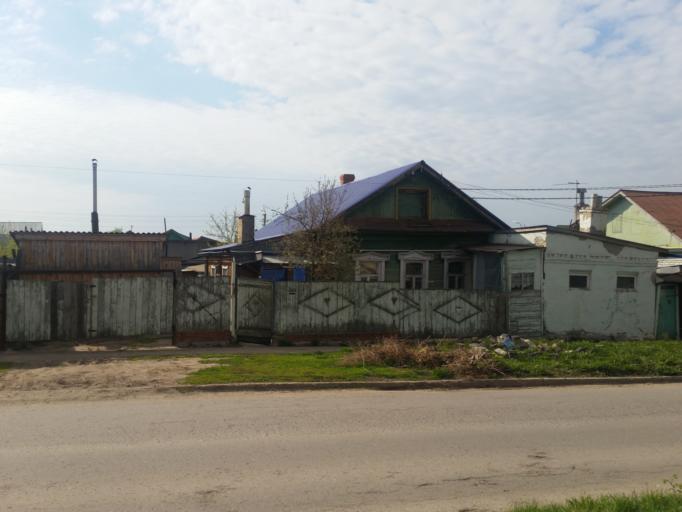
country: RU
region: Ulyanovsk
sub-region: Ulyanovskiy Rayon
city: Ulyanovsk
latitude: 54.3384
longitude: 48.3752
